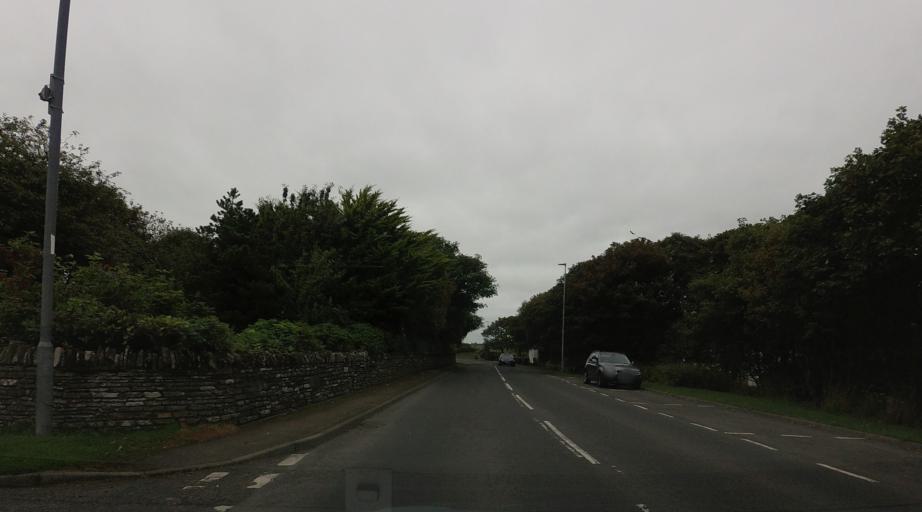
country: GB
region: Scotland
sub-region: Orkney Islands
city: Orkney
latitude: 59.0083
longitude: -3.1229
